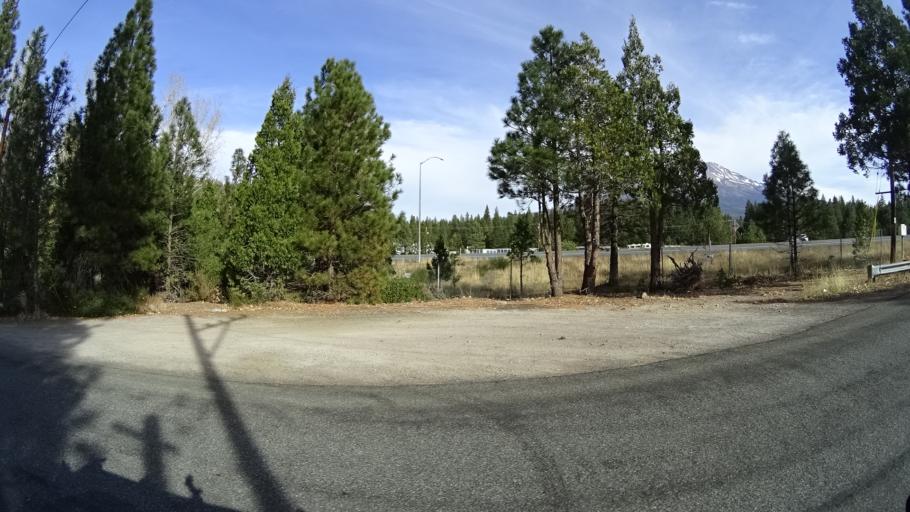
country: US
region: California
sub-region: Siskiyou County
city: Weed
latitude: 41.4098
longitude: -122.3807
